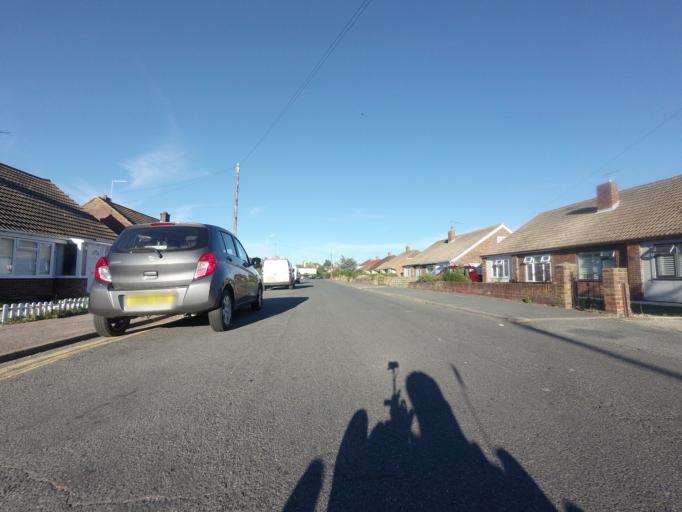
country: GB
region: England
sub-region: Kent
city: Herne Bay
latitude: 51.3588
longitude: 1.1535
